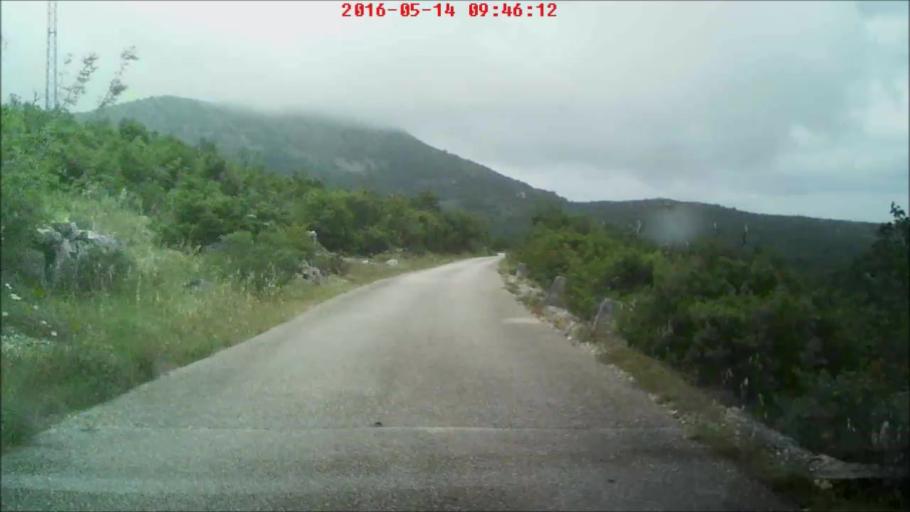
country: HR
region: Dubrovacko-Neretvanska
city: Podgora
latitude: 42.7791
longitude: 17.9132
